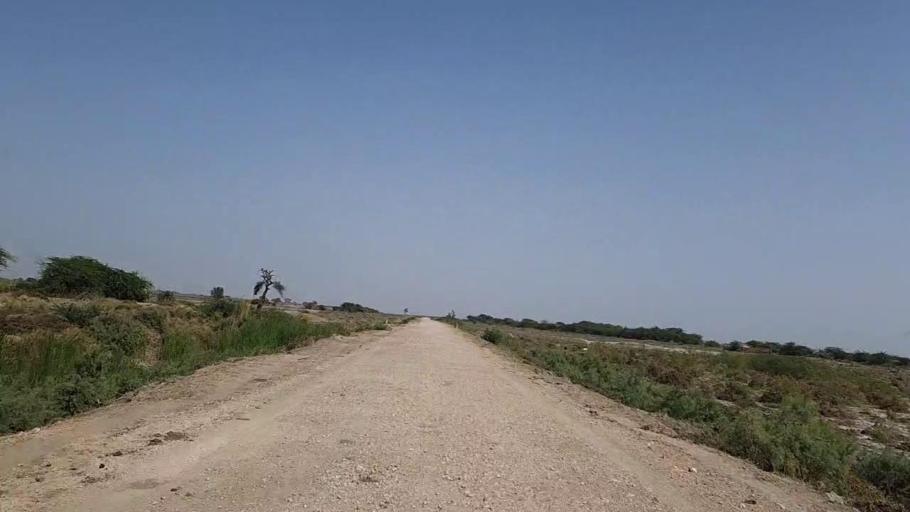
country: PK
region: Sindh
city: Jati
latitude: 24.3608
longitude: 68.2852
